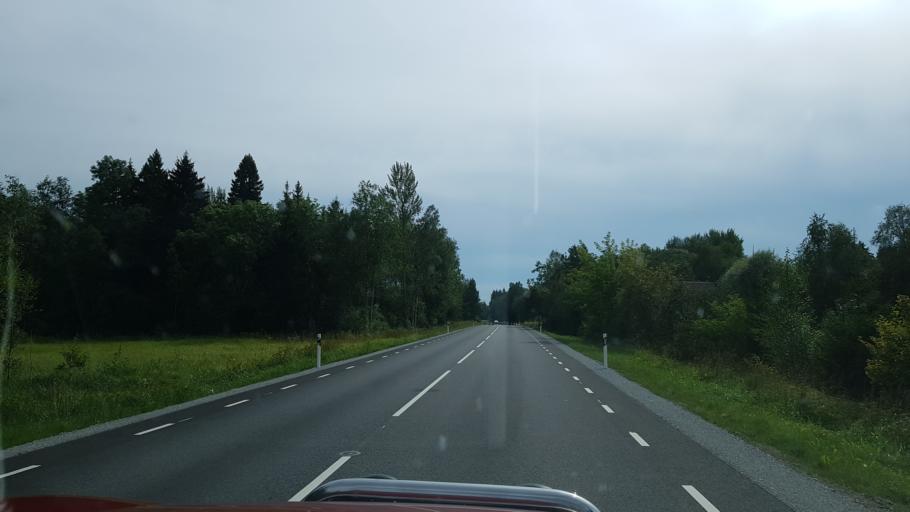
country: EE
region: Laeaene
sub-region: Ridala Parish
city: Uuemoisa
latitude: 59.0481
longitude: 23.8784
